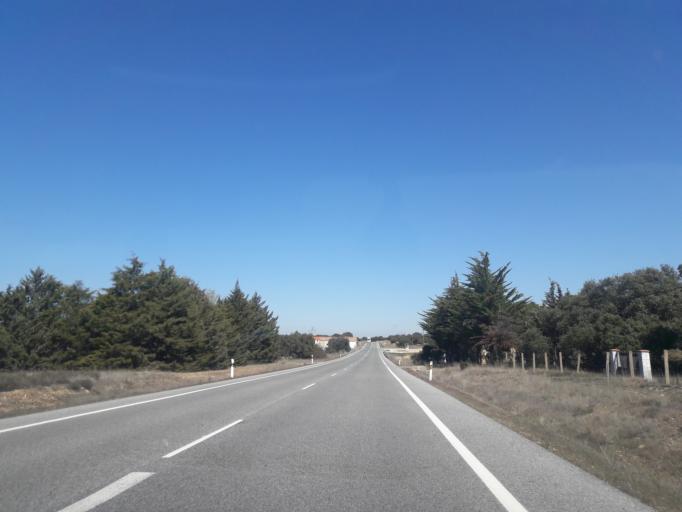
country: ES
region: Castille and Leon
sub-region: Provincia de Salamanca
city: Mozarbez
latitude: 40.8297
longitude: -5.6386
